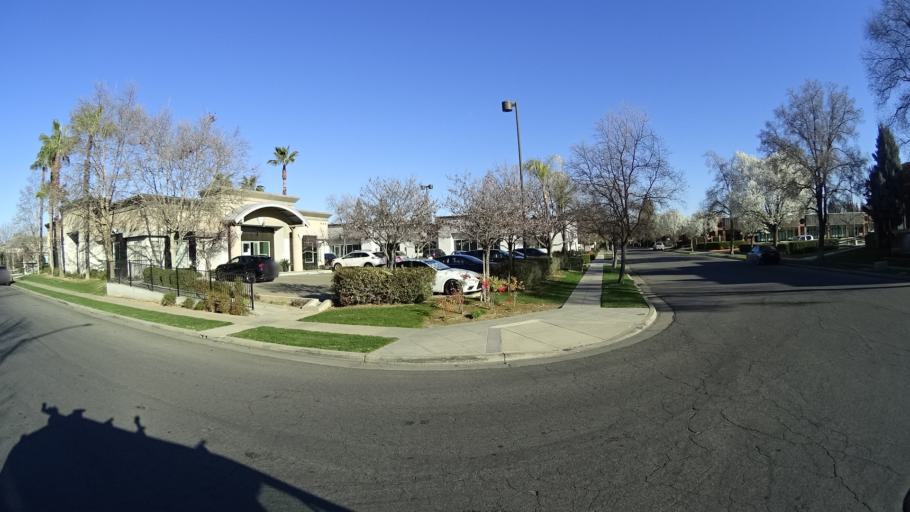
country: US
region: California
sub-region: Fresno County
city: Clovis
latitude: 36.8383
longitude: -119.7424
